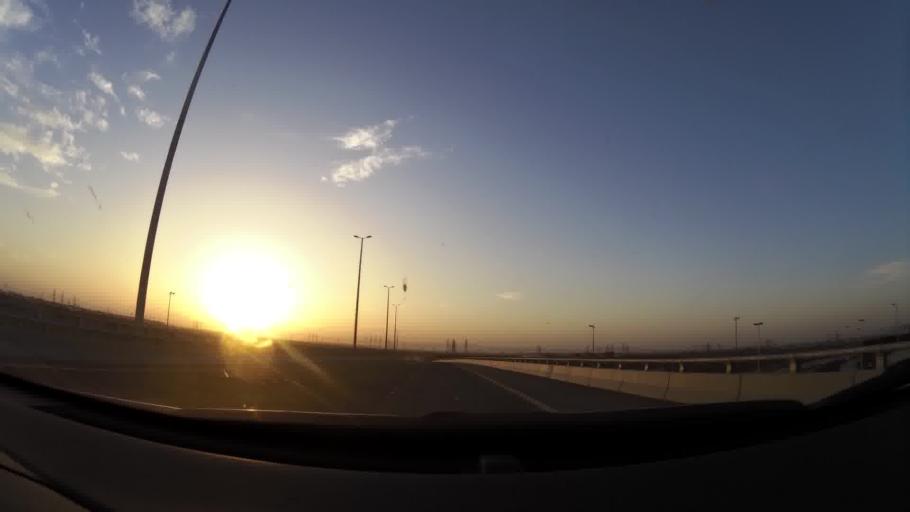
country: KW
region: Al Asimah
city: Ar Rabiyah
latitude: 29.3202
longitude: 47.8037
